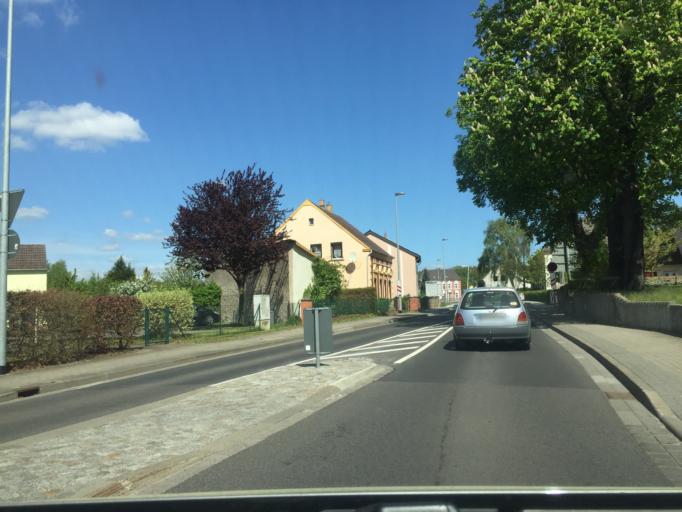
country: DE
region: Mecklenburg-Vorpommern
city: Torgelow
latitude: 53.6347
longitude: 14.0132
